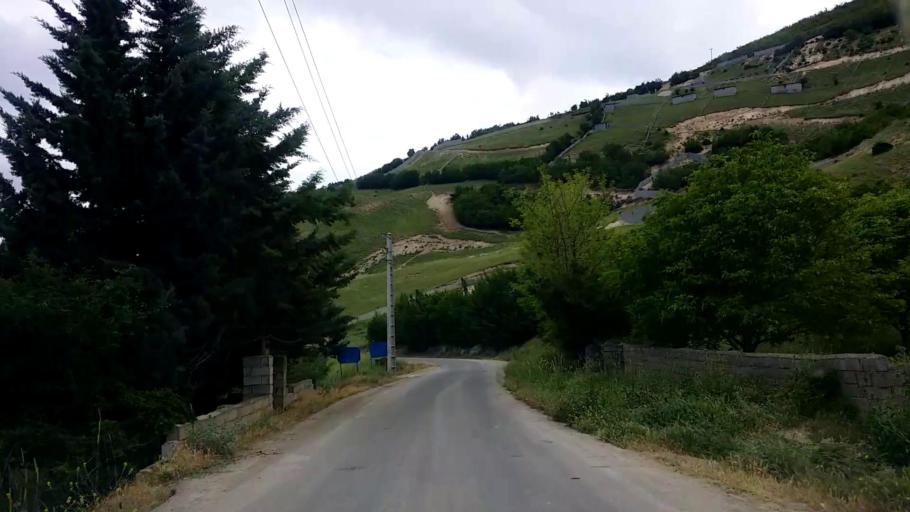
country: IR
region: Mazandaran
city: Chalus
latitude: 36.5451
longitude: 51.2712
